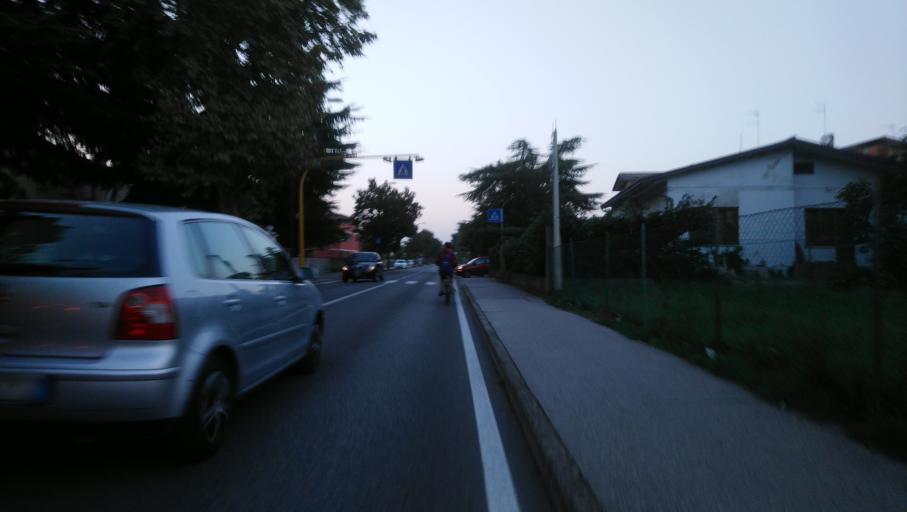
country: IT
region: Veneto
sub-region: Provincia di Treviso
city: Treviso
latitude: 45.6866
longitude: 12.2174
